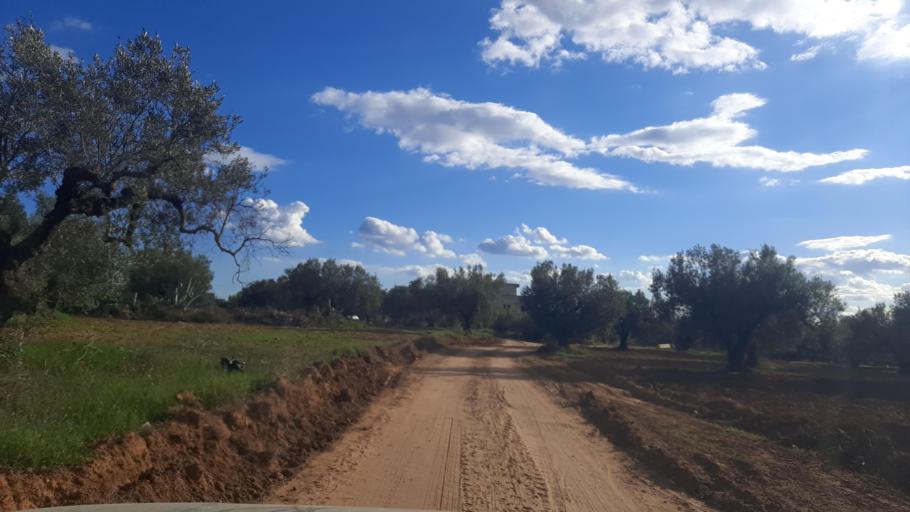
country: TN
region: Nabul
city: Al Hammamat
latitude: 36.4287
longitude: 10.5064
